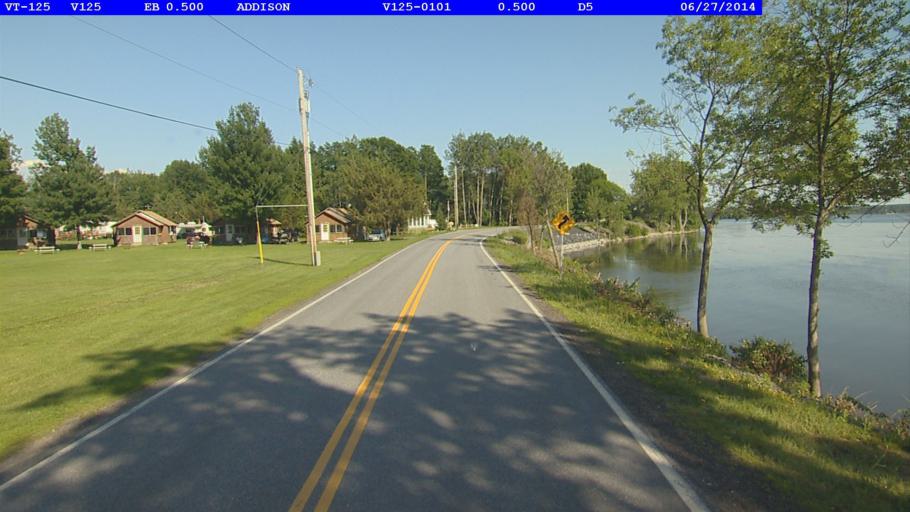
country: US
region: New York
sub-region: Essex County
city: Port Henry
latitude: 44.0328
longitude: -73.4097
